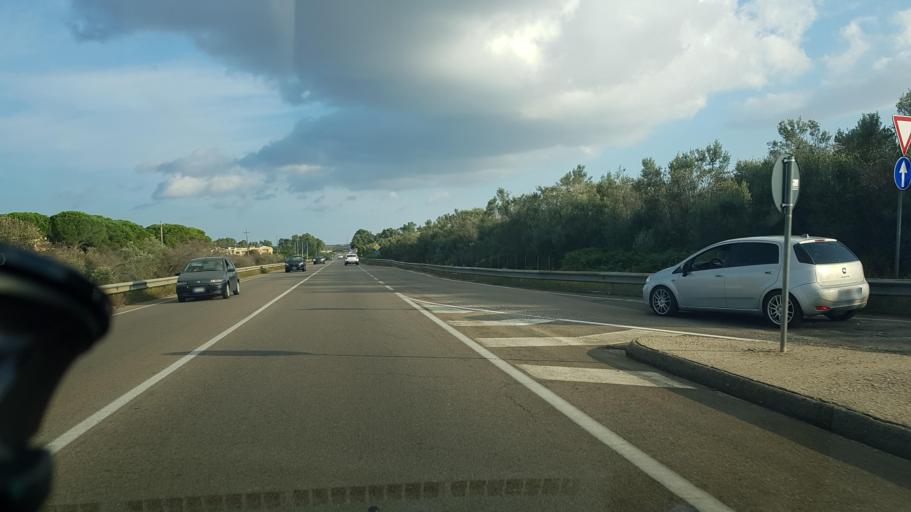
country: IT
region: Apulia
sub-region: Provincia di Lecce
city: Acquarica del Capo
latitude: 39.8996
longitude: 18.2508
